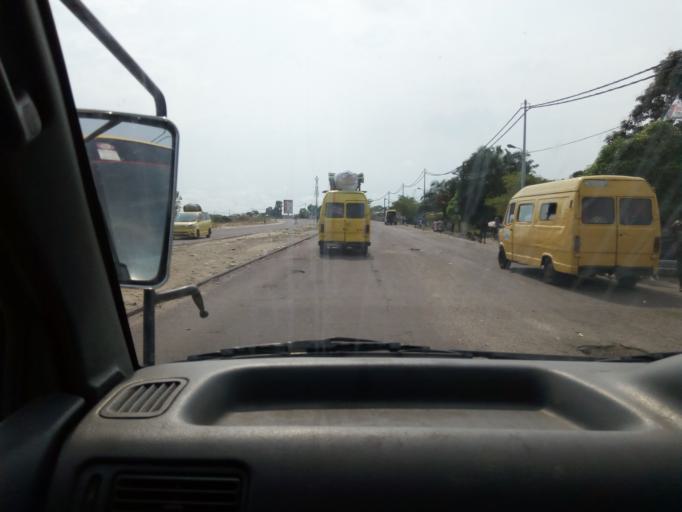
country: CD
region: Kinshasa
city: Masina
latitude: -4.3857
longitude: 15.4666
